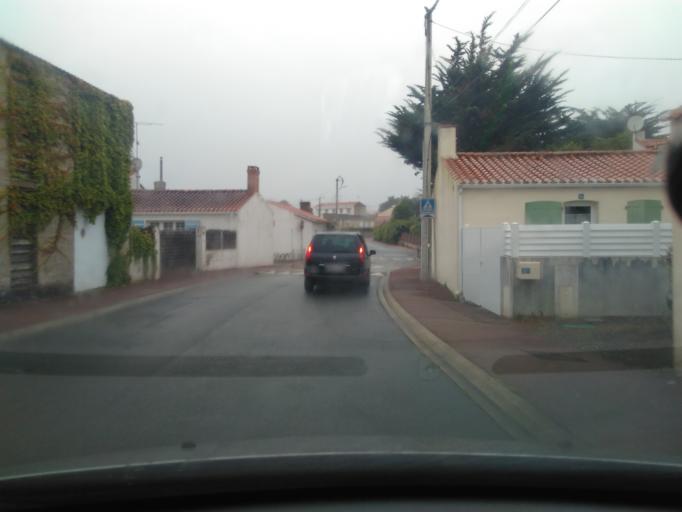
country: FR
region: Pays de la Loire
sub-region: Departement de la Vendee
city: Bretignolles-sur-Mer
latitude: 46.6303
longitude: -1.8571
